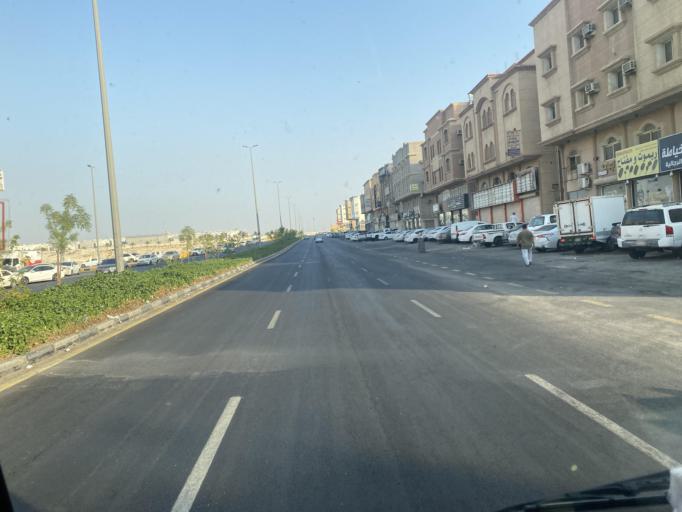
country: SA
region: Eastern Province
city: Dhahran
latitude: 26.3534
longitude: 50.0488
